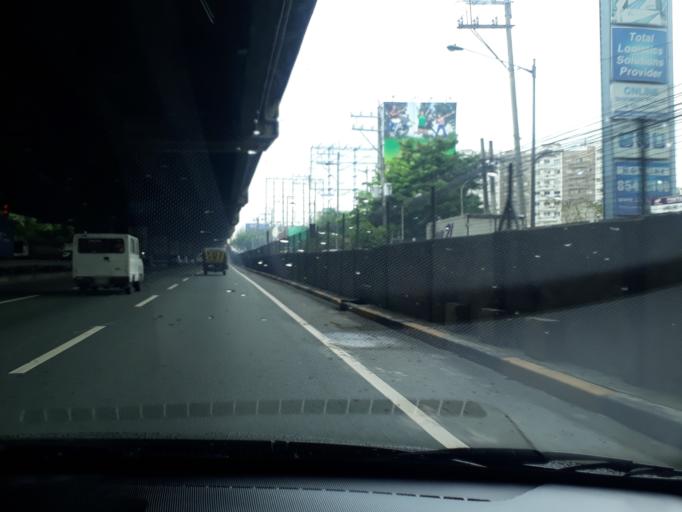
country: PH
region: Calabarzon
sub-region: Province of Rizal
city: Taguig
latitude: 14.5021
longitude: 121.0374
